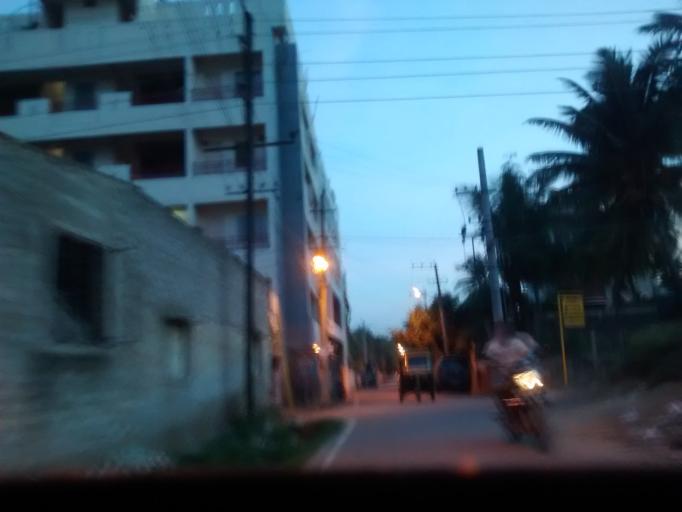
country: IN
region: Karnataka
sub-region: Bangalore Urban
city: Bangalore
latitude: 12.9682
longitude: 77.6680
